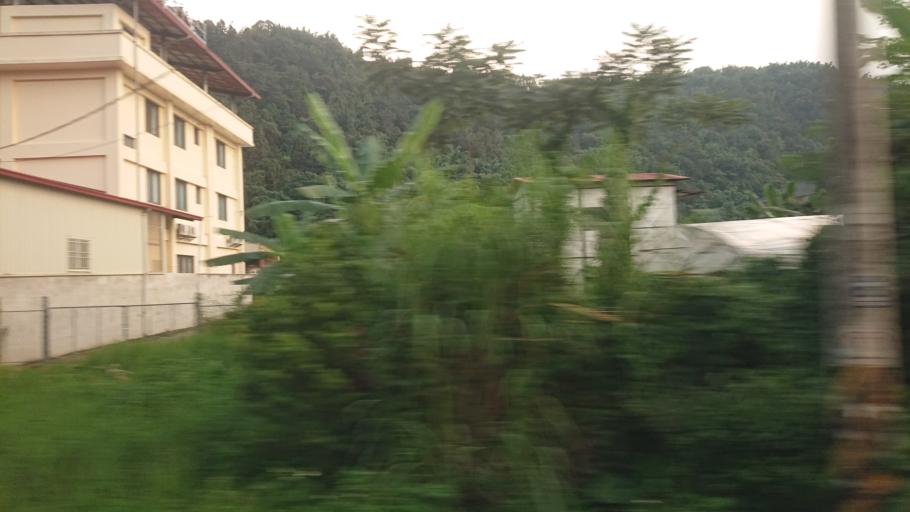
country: TW
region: Taiwan
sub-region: Nantou
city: Puli
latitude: 23.9727
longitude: 120.9948
